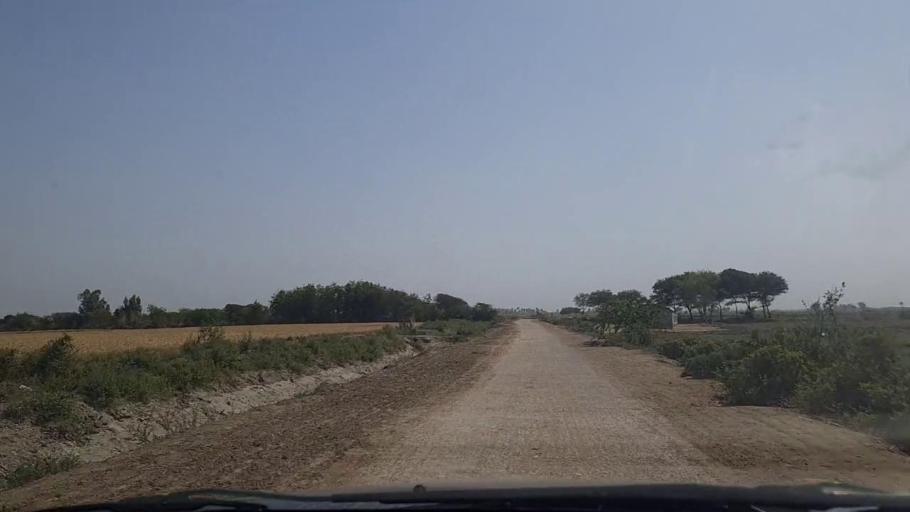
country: PK
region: Sindh
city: Keti Bandar
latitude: 24.2712
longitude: 67.6723
